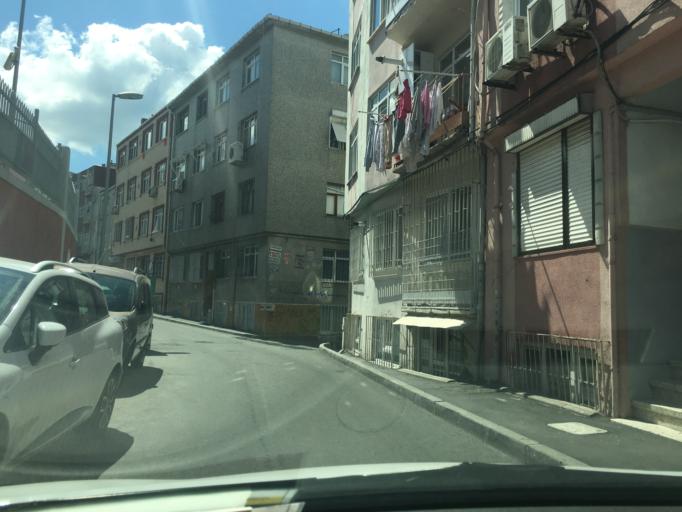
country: TR
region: Istanbul
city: Istanbul
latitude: 41.0102
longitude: 28.9256
